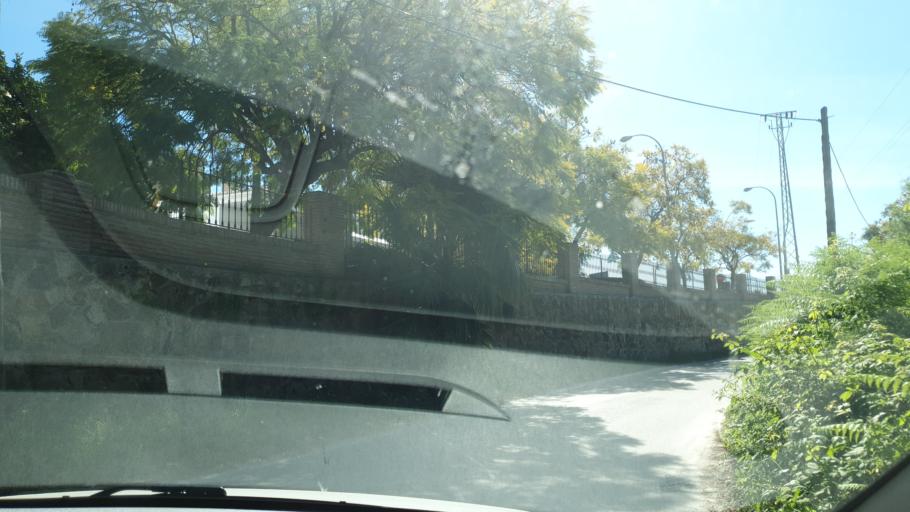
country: ES
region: Andalusia
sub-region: Provincia de Malaga
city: Marbella
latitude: 36.5292
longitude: -4.8821
